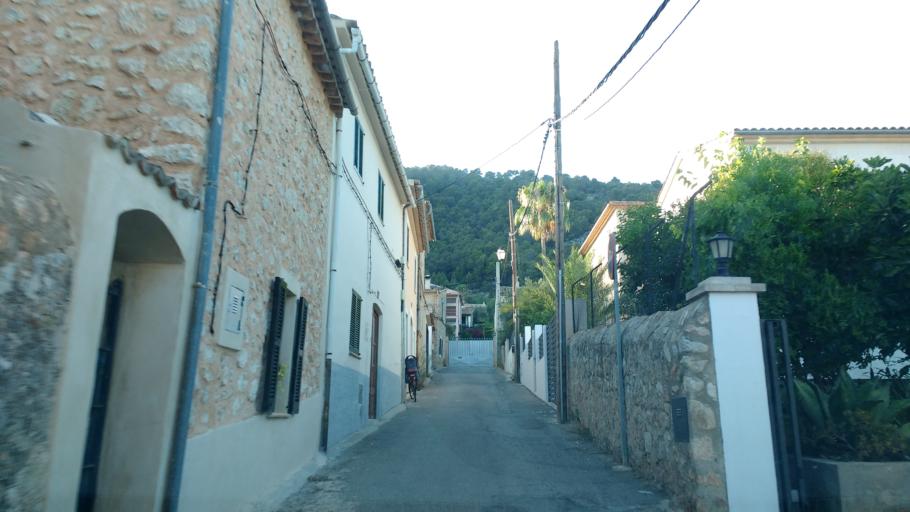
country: ES
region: Balearic Islands
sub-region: Illes Balears
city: Alaro
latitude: 39.7089
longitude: 2.7916
